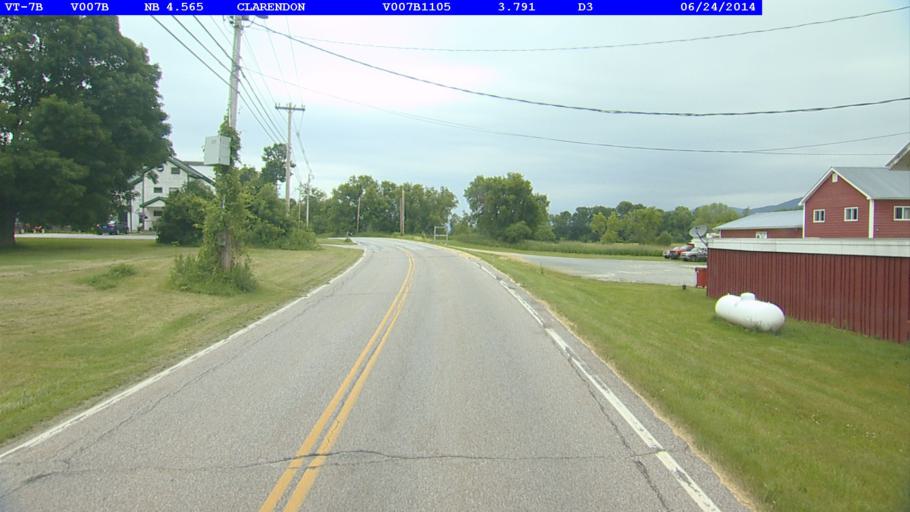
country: US
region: Vermont
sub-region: Rutland County
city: Rutland
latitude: 43.5532
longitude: -72.9582
